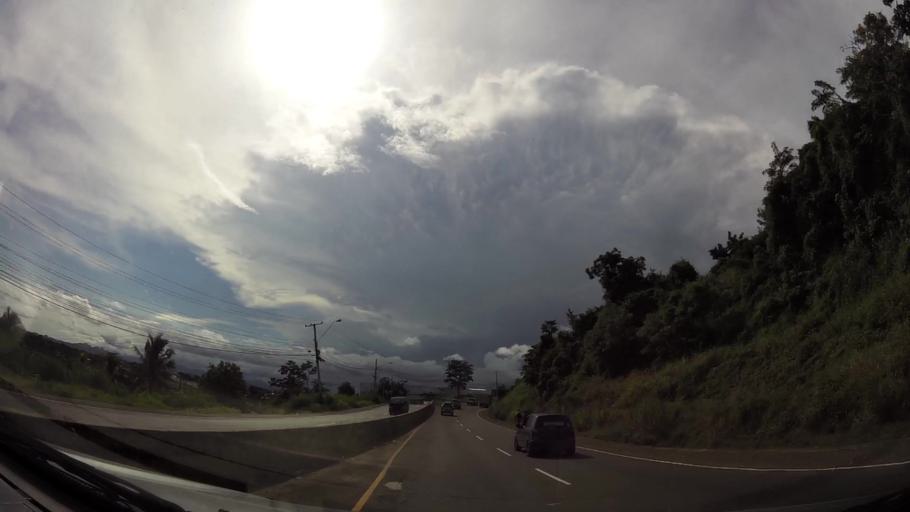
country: PA
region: Panama
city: La Chorrera
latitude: 8.8894
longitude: -79.7673
